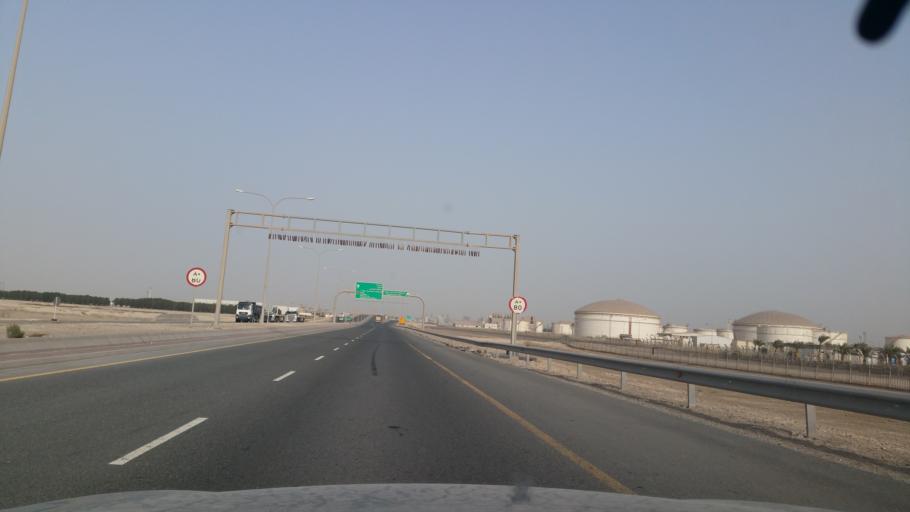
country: QA
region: Al Wakrah
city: Umm Sa'id
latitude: 24.9740
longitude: 51.5425
